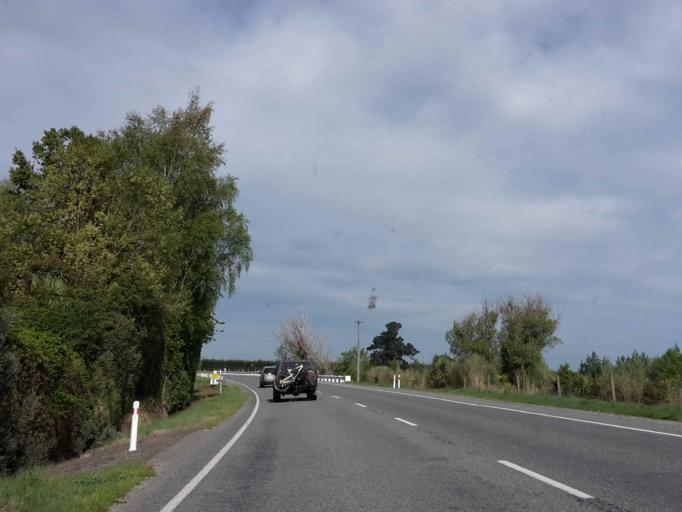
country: NZ
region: Canterbury
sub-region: Timaru District
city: Pleasant Point
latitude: -44.1174
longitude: 171.1771
